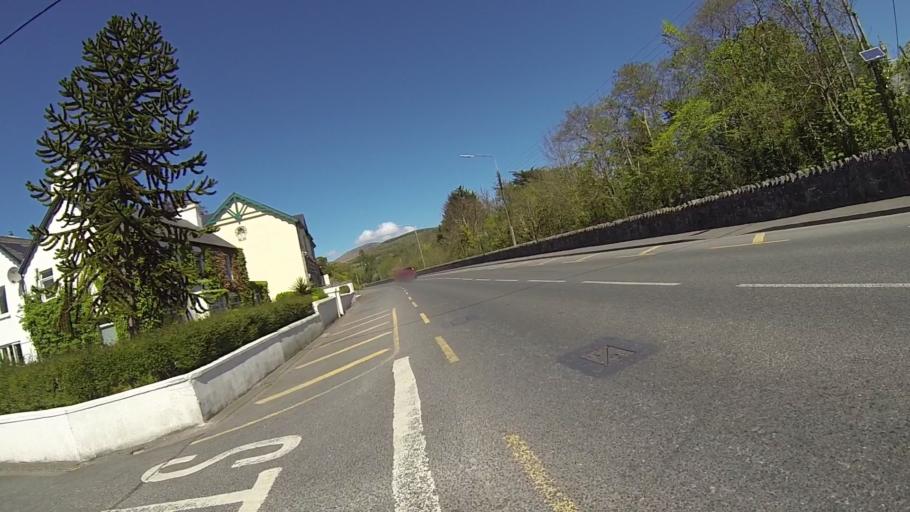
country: IE
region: Munster
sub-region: Ciarrai
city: Kenmare
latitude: 51.8814
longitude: -9.5848
